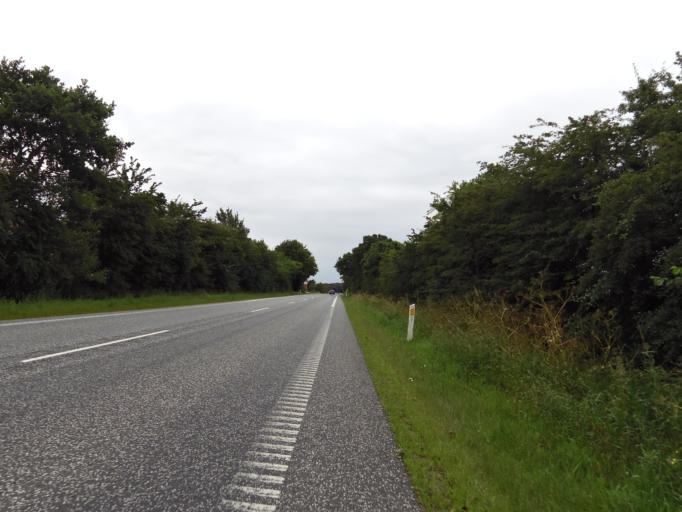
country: DK
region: South Denmark
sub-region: Tonder Kommune
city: Logumkloster
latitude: 55.1018
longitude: 8.9422
